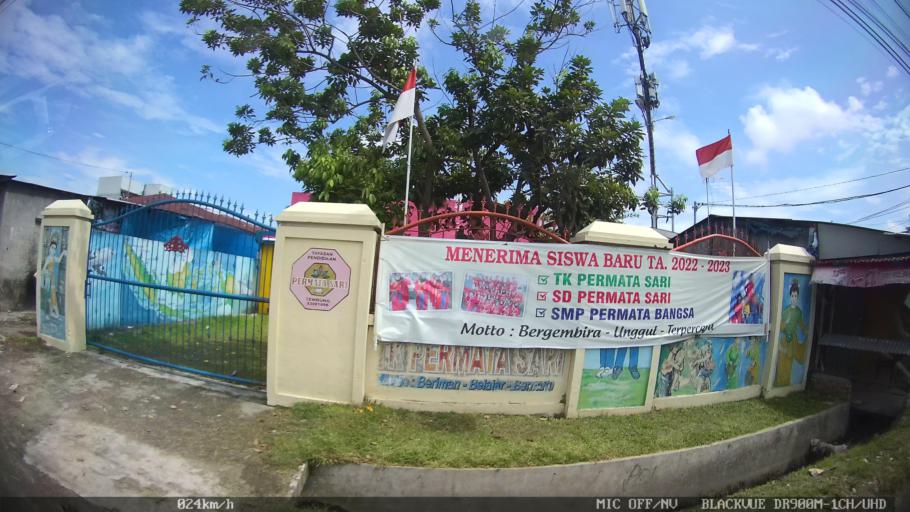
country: ID
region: North Sumatra
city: Medan
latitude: 3.5910
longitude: 98.7504
